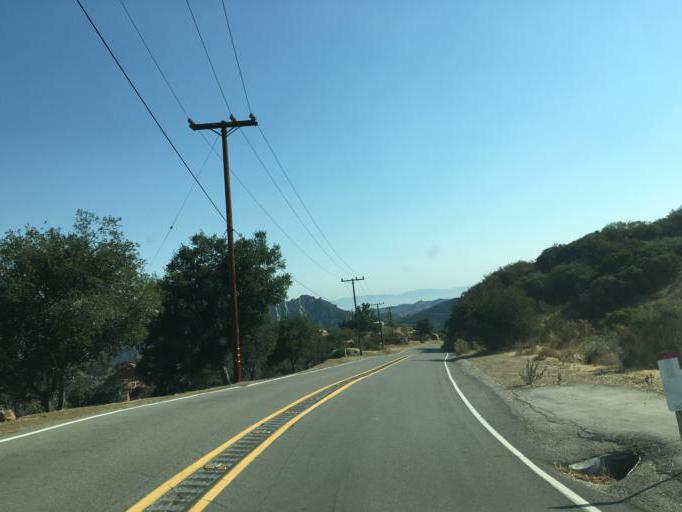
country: US
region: California
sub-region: Los Angeles County
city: Las Flores
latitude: 34.0871
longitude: -118.6650
